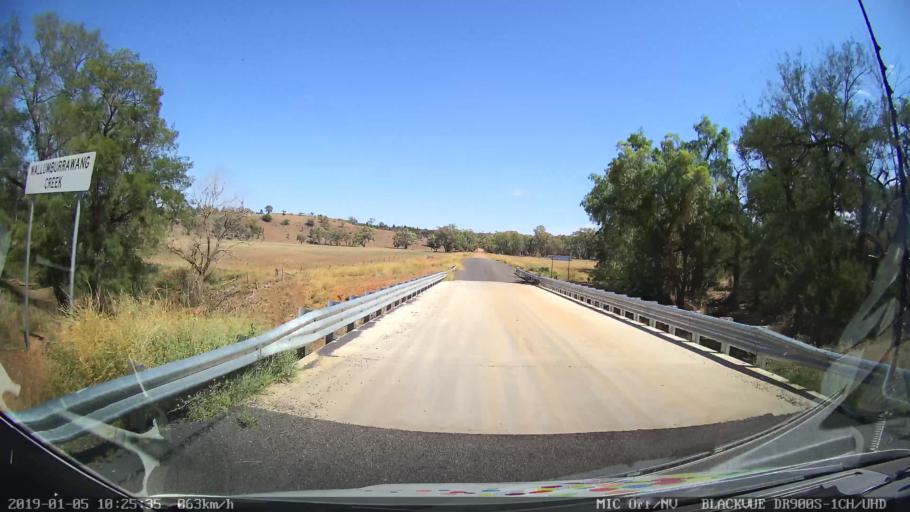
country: AU
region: New South Wales
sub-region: Gilgandra
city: Gilgandra
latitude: -31.5603
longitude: 148.9588
